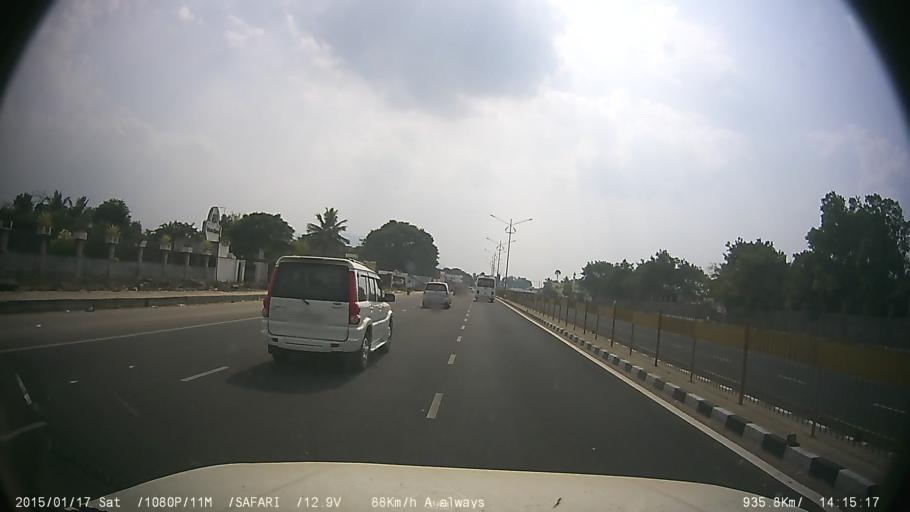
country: IN
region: Tamil Nadu
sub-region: Vellore
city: Ambur
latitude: 12.7676
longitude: 78.7076
